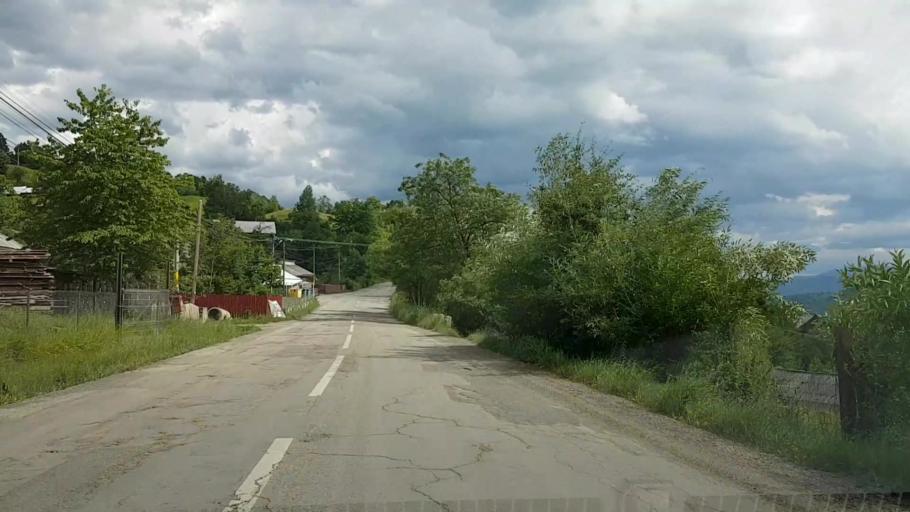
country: RO
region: Neamt
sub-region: Comuna Hangu
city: Hangu
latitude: 47.0429
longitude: 26.0549
